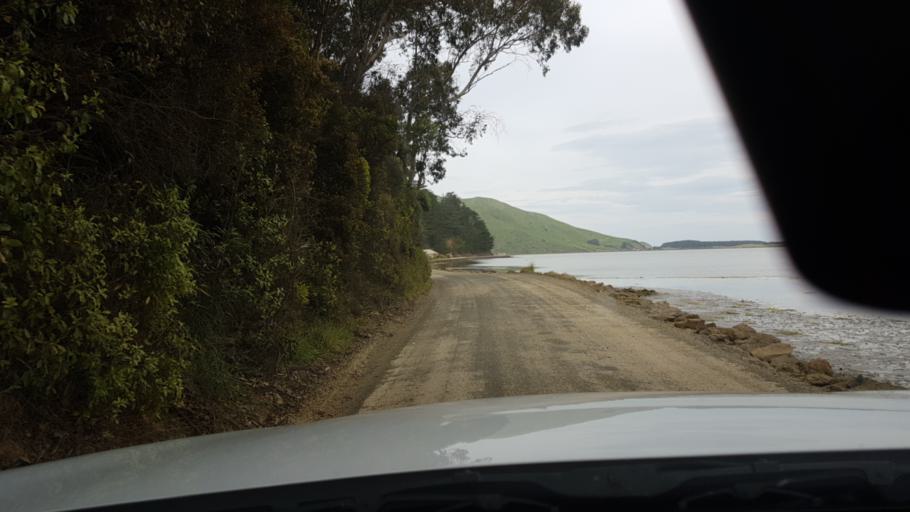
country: NZ
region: Otago
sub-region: Dunedin City
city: Portobello
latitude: -45.8528
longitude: 170.6655
